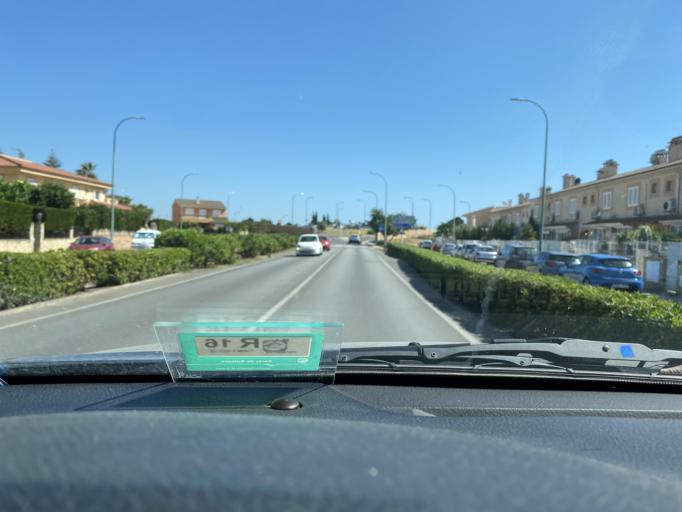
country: ES
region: Balearic Islands
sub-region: Illes Balears
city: Palma
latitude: 39.6084
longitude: 2.6854
